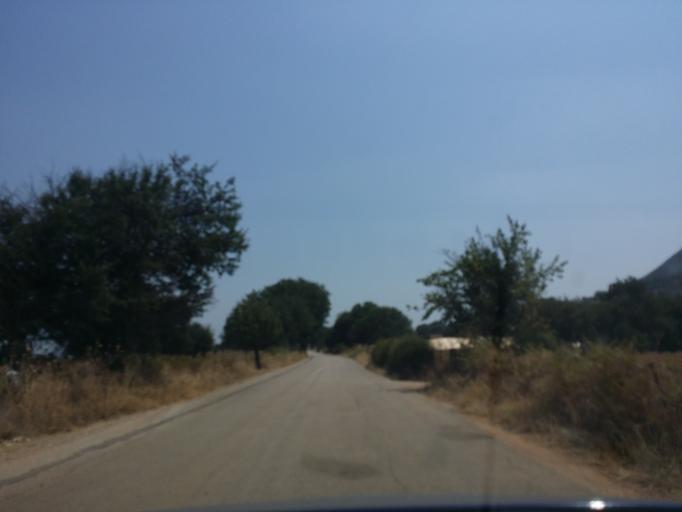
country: GR
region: West Greece
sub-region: Nomos Aitolias kai Akarnanias
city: Archontochorion
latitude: 38.6962
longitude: 21.1027
